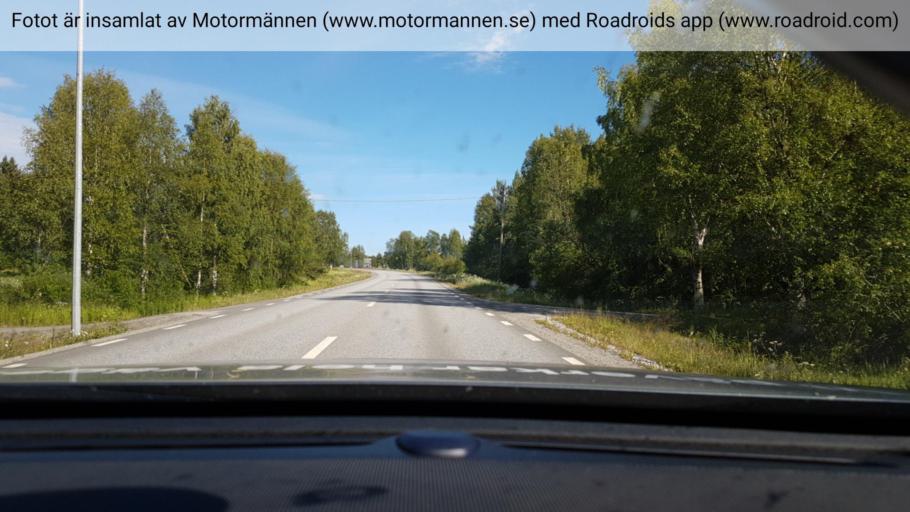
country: SE
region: Vaesterbotten
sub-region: Lycksele Kommun
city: Lycksele
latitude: 64.6987
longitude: 18.3713
